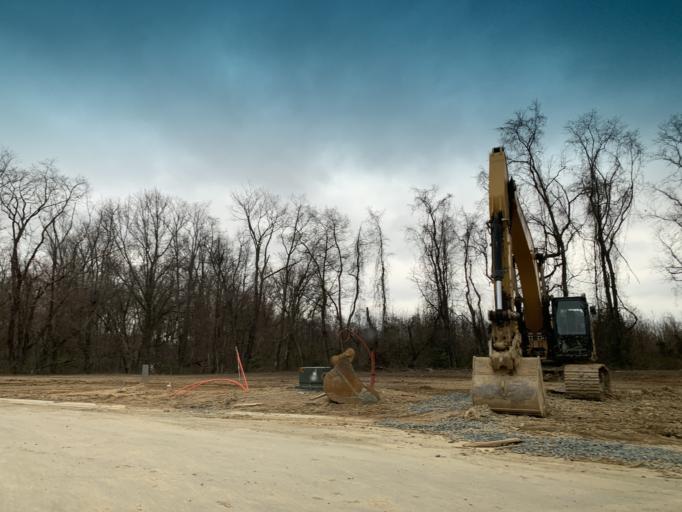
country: US
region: Maryland
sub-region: Harford County
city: Aberdeen
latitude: 39.5401
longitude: -76.1896
